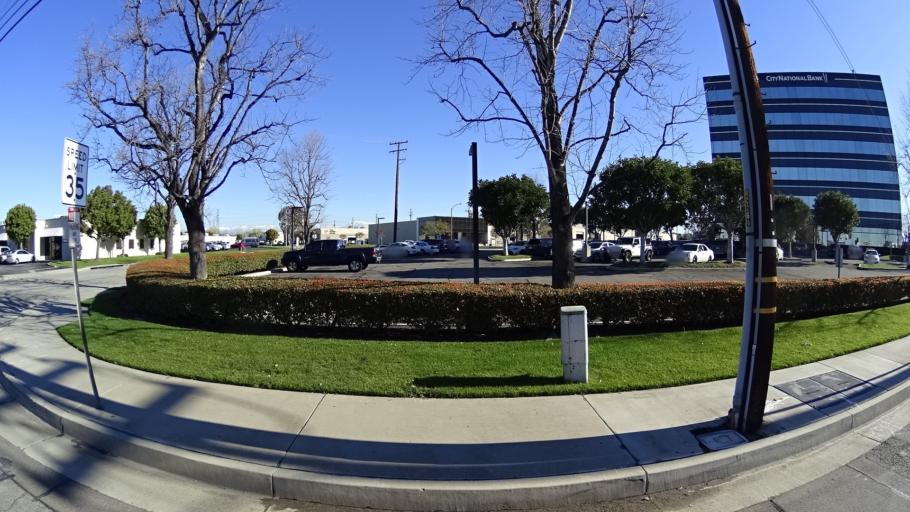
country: US
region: California
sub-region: Orange County
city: Orange
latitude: 33.8063
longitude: -117.8842
